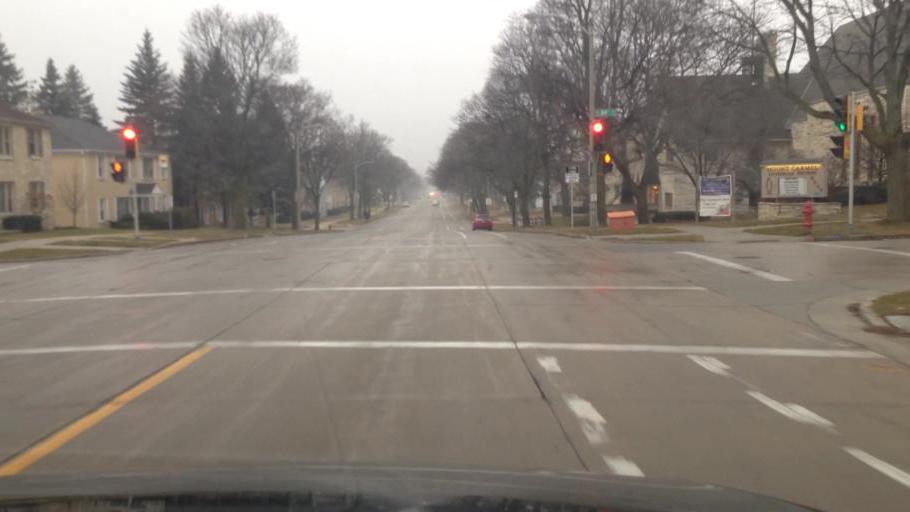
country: US
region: Wisconsin
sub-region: Milwaukee County
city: Wauwatosa
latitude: 43.0679
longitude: -88.0172
